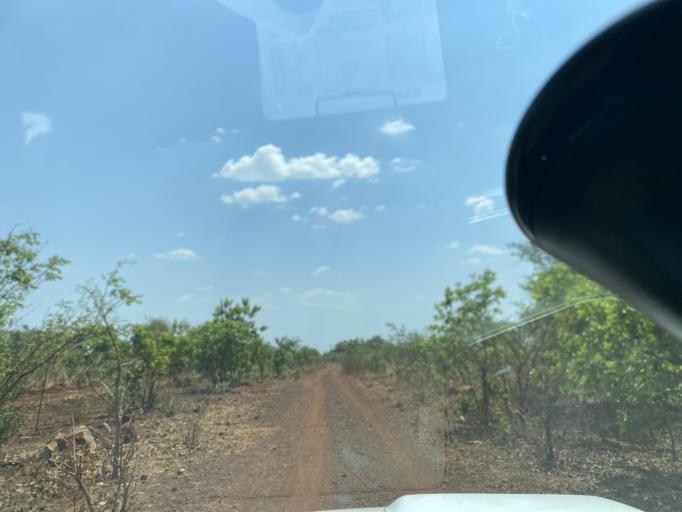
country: ZM
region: Lusaka
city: Lusaka
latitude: -15.4977
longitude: 27.9656
